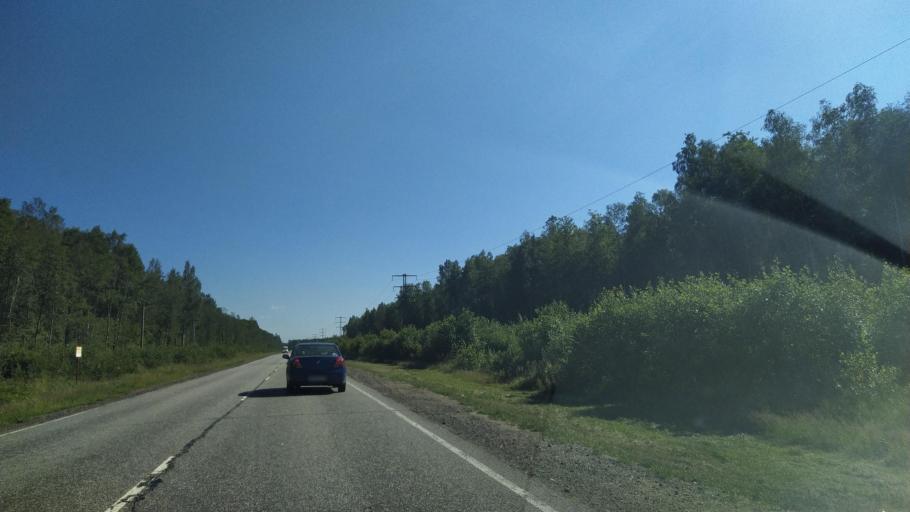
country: RU
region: Leningrad
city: Imeni Morozova
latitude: 60.0421
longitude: 31.0358
